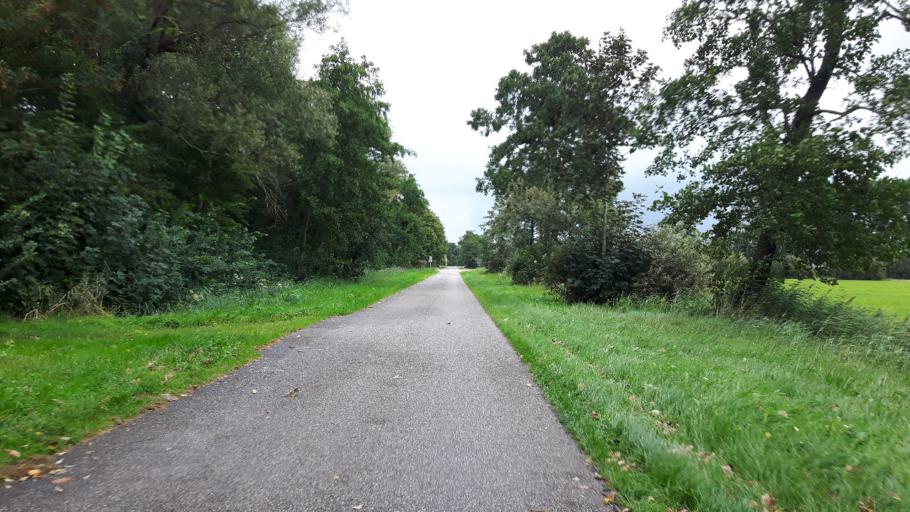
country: NL
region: Friesland
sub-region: Gemeente Dantumadiel
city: Broeksterwald
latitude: 53.2693
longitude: 5.9829
